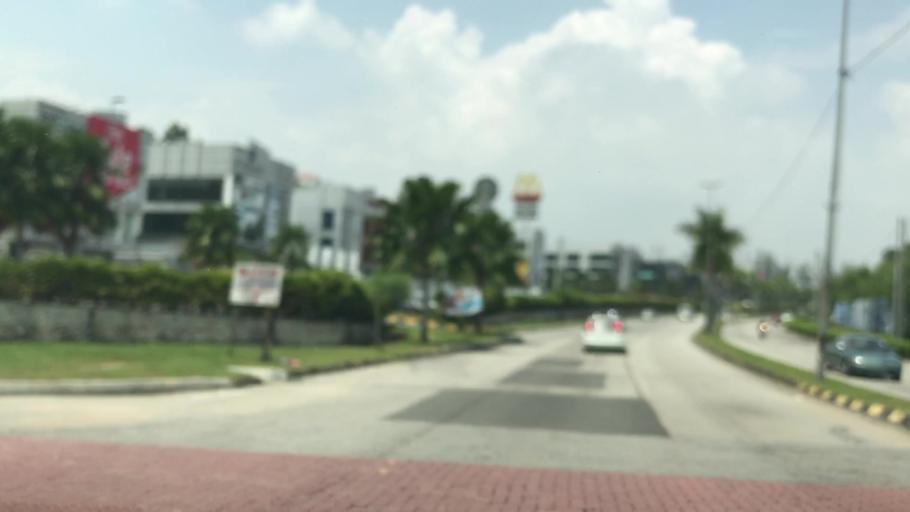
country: MY
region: Selangor
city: Subang Jaya
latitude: 3.0214
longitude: 101.6241
